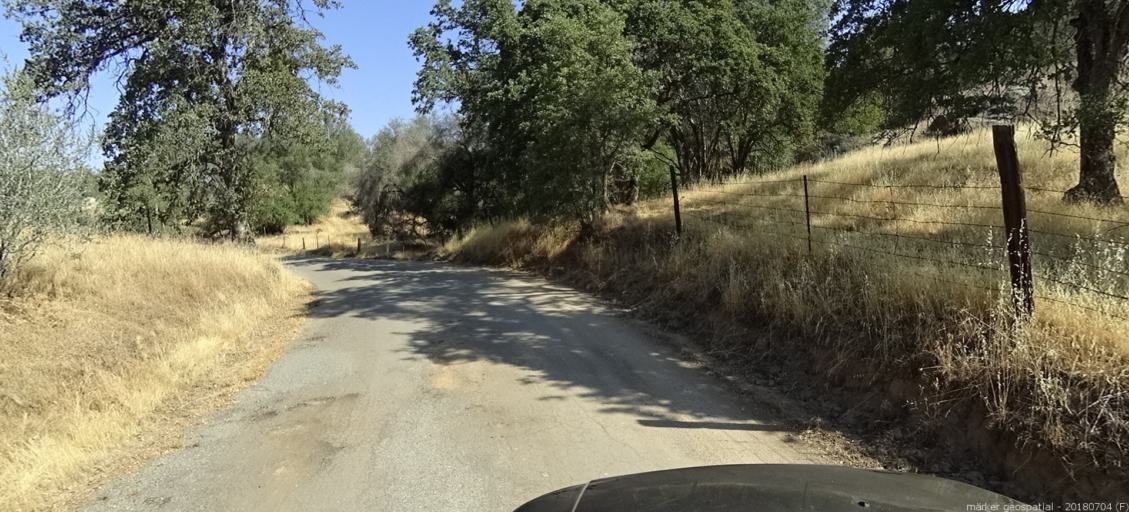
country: US
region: California
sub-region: Fresno County
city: Auberry
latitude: 37.1027
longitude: -119.6224
